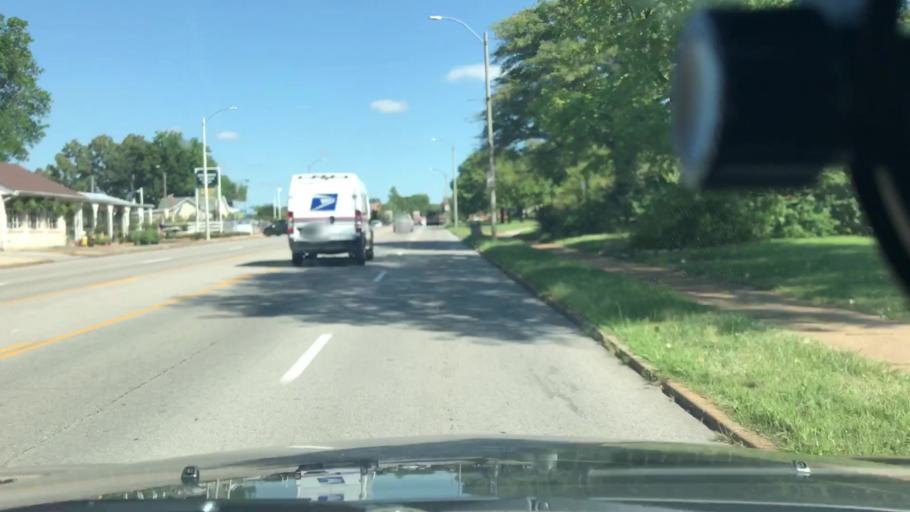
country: US
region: Missouri
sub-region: Saint Louis County
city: Maplewood
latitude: 38.6003
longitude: -90.2921
